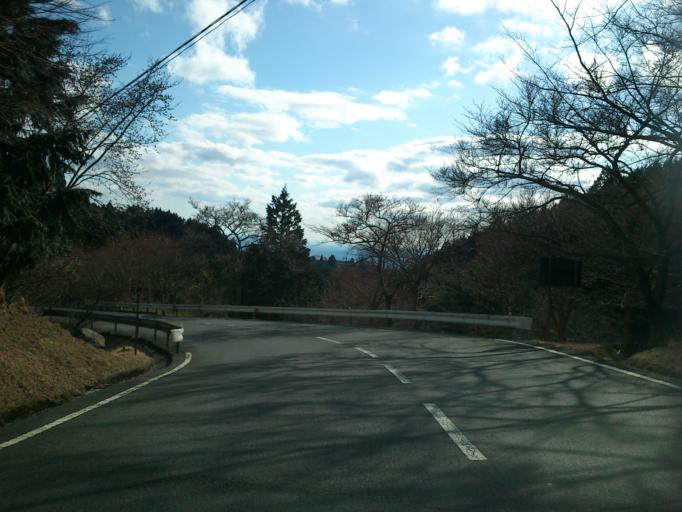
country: JP
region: Shiga Prefecture
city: Otsu-shi
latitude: 35.0604
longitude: 135.8357
